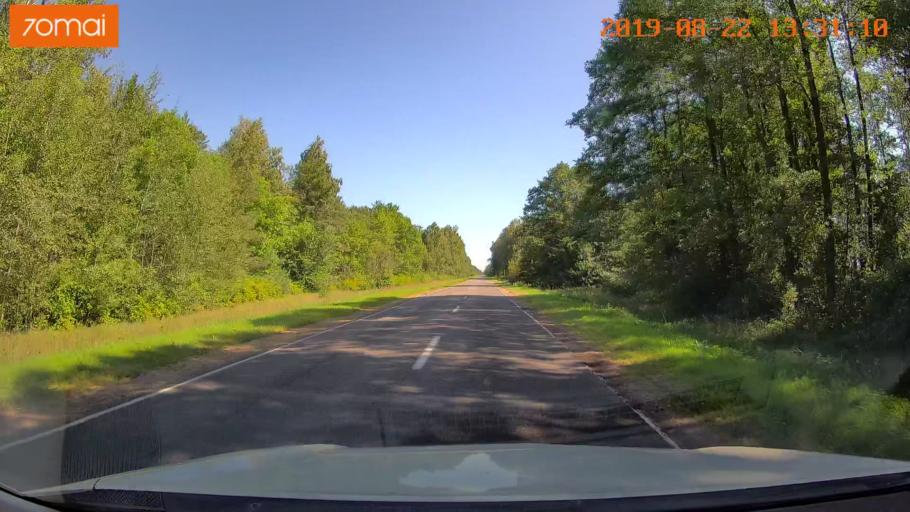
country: BY
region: Minsk
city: Staryya Darohi
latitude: 53.2173
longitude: 28.1728
